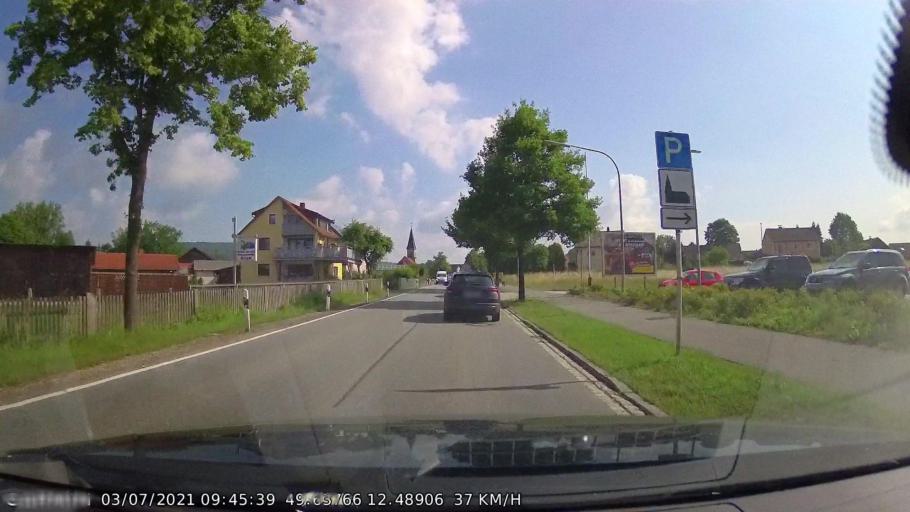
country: DE
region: Bavaria
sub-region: Upper Palatinate
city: Waidhaus
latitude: 49.6377
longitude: 12.4891
